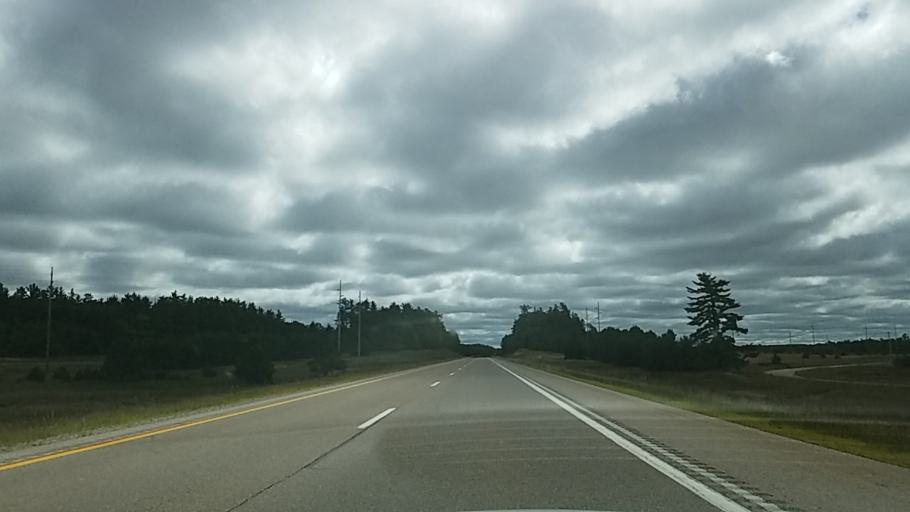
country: US
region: Michigan
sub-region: Roscommon County
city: Roscommon
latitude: 44.5400
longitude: -84.6923
